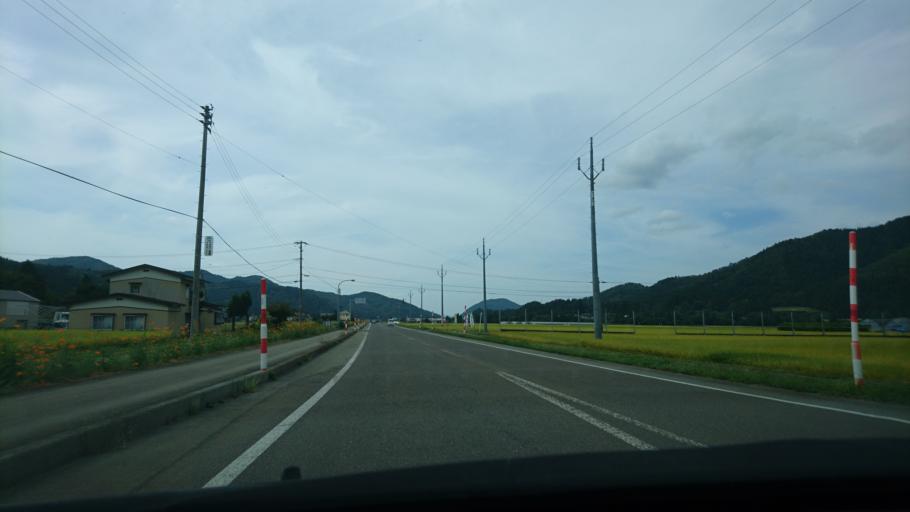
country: JP
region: Akita
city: Yuzawa
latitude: 39.1822
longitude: 140.6484
